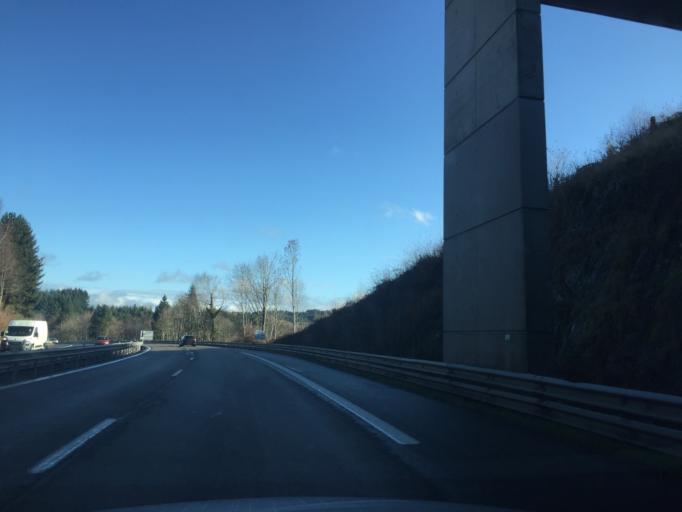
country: FR
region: Auvergne
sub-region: Departement du Puy-de-Dome
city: Saint-Remy-sur-Durolle
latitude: 45.8820
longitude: 3.5919
